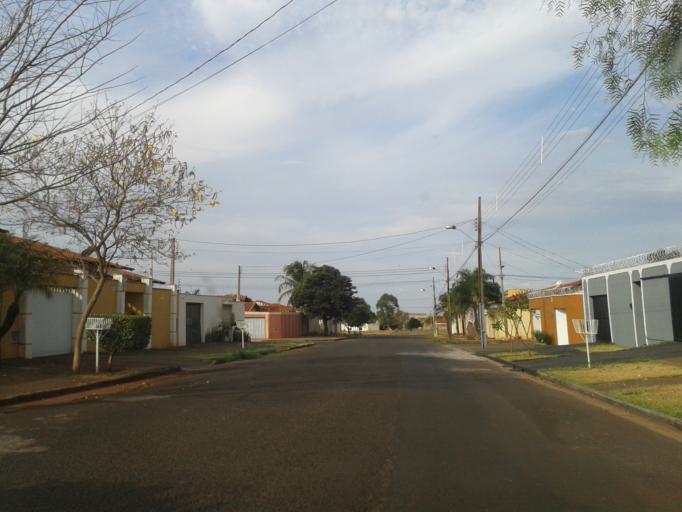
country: BR
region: Minas Gerais
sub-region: Ituiutaba
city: Ituiutaba
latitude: -18.9912
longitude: -49.4547
